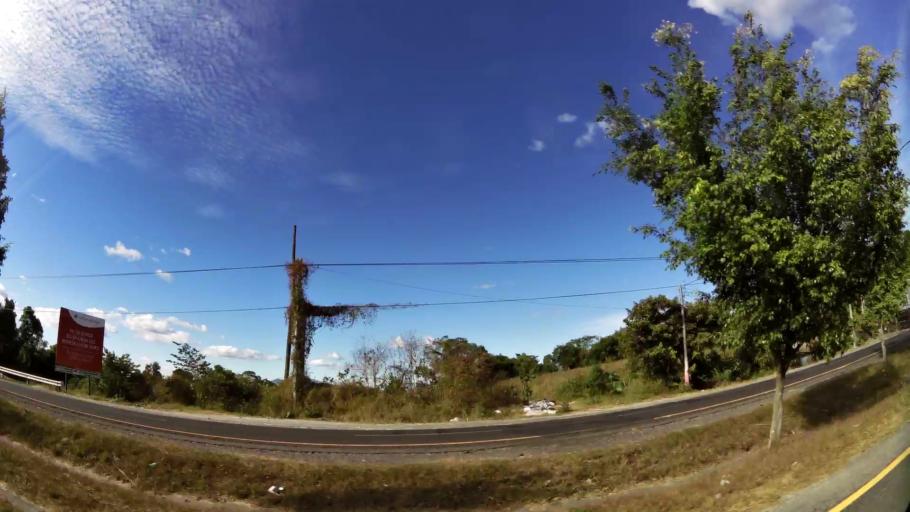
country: SV
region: Cuscatlan
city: Tecoluca
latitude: 13.7366
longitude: -89.0460
